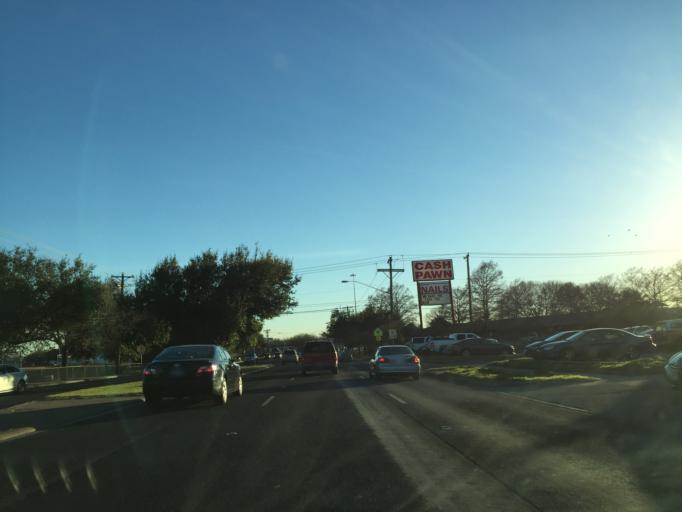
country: US
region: Texas
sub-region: Travis County
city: Austin
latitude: 30.3247
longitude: -97.6932
